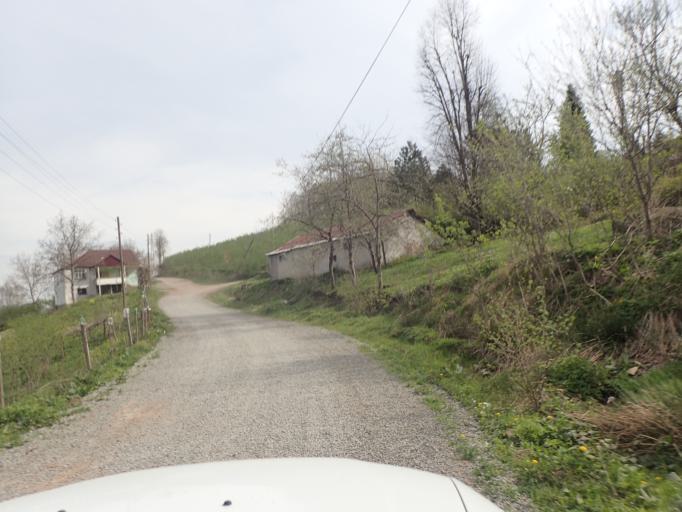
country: TR
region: Ordu
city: Aybasti
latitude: 40.7207
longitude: 37.2909
